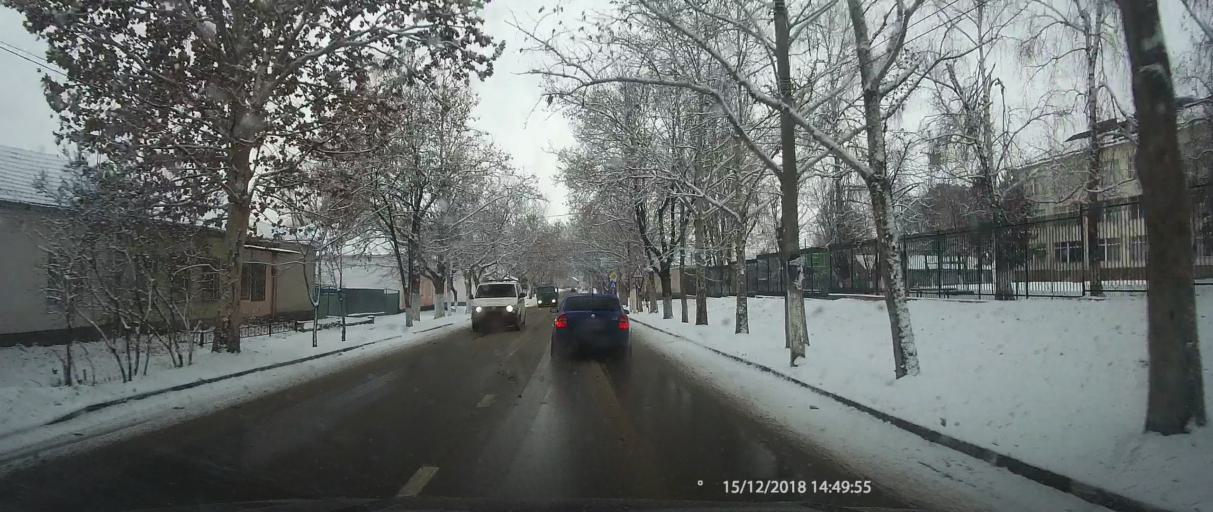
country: MD
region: Cahul
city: Cahul
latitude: 45.9023
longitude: 28.1929
